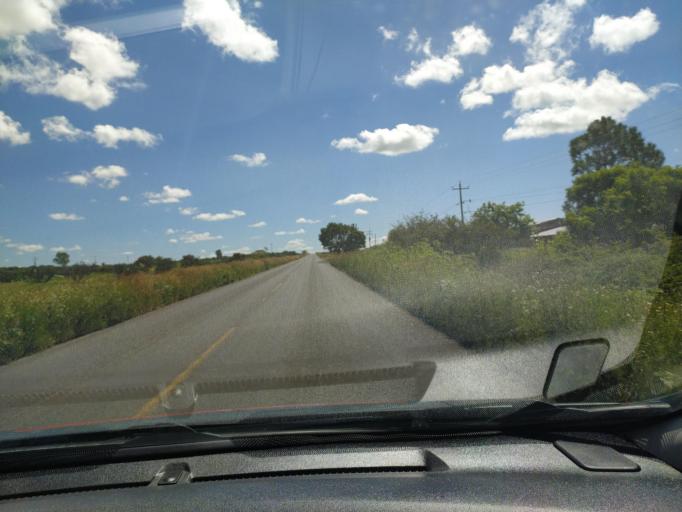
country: MX
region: Jalisco
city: Valle de Guadalupe
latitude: 21.0215
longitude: -102.5364
